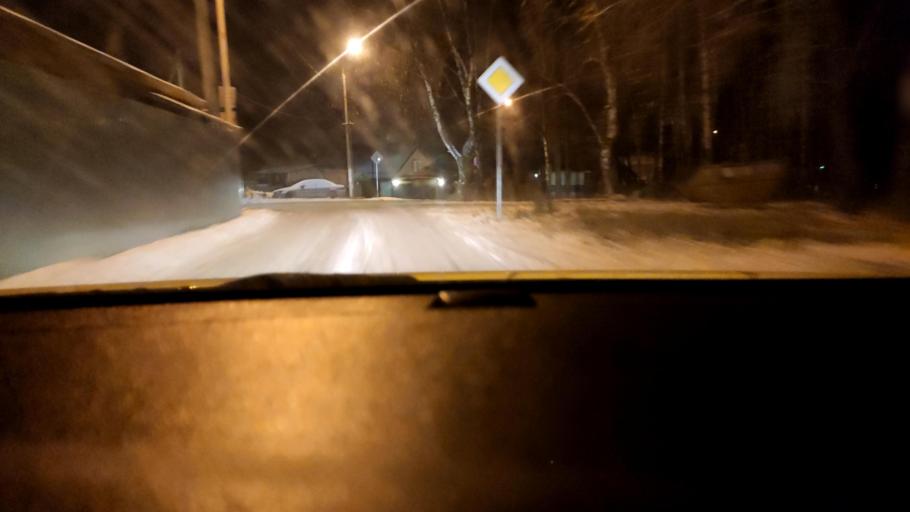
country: RU
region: Tatarstan
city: Osinovo
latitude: 55.8314
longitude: 48.8618
